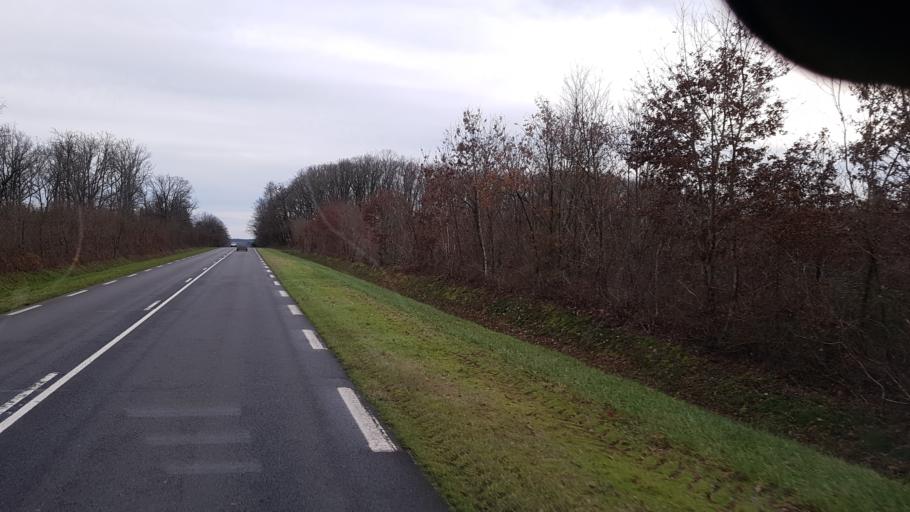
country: FR
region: Centre
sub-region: Departement du Loir-et-Cher
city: Lamotte-Beuvron
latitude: 47.6203
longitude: 2.0133
